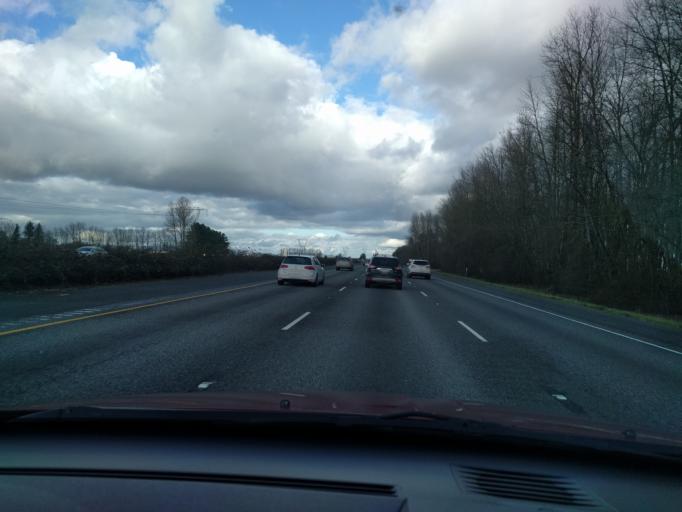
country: US
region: Oregon
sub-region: Marion County
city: Hayesville
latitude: 45.0629
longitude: -122.9654
